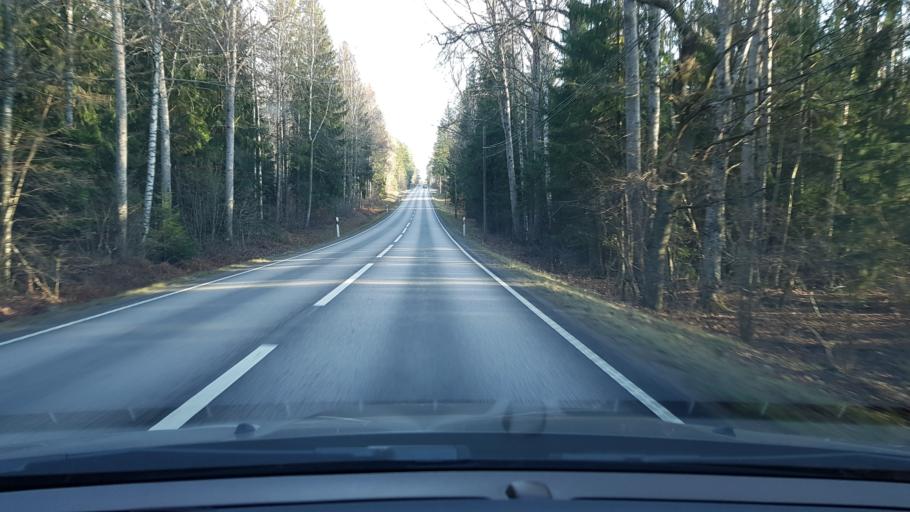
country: SE
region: Stockholm
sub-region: Norrtalje Kommun
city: Rimbo
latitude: 59.7406
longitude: 18.3156
